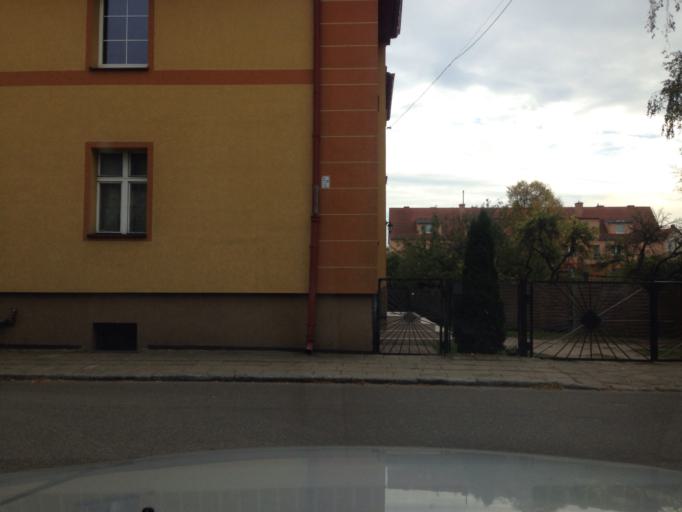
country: PL
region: Pomeranian Voivodeship
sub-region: Powiat leborski
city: Lebork
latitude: 54.5312
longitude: 17.7600
